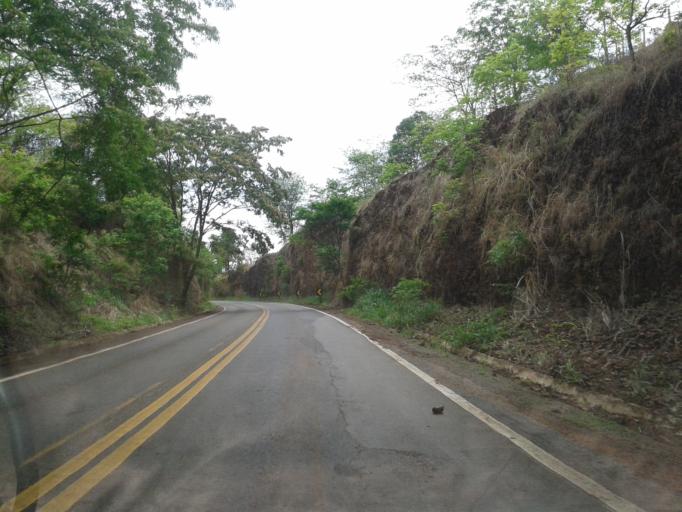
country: BR
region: Goias
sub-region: Buriti Alegre
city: Buriti Alegre
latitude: -18.1388
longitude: -48.9530
